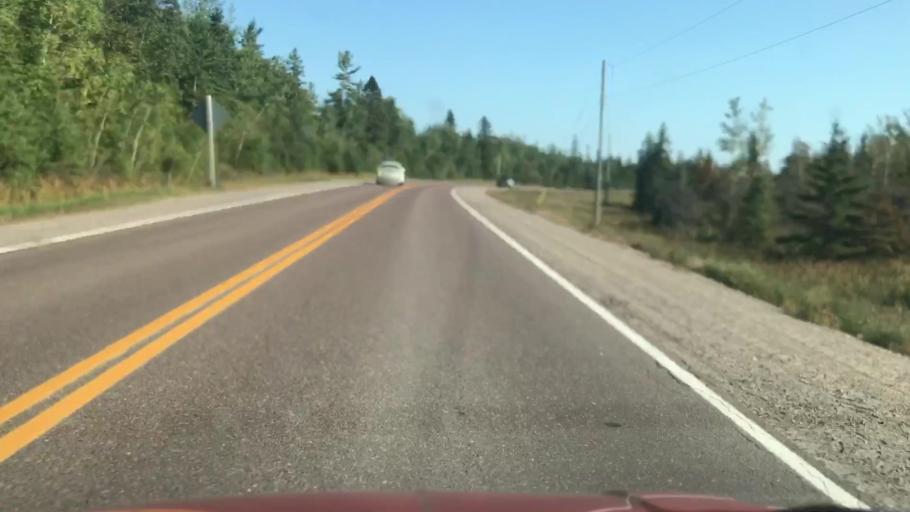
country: CA
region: Ontario
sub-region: Algoma
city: Sault Ste. Marie
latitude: 46.3355
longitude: -84.0072
